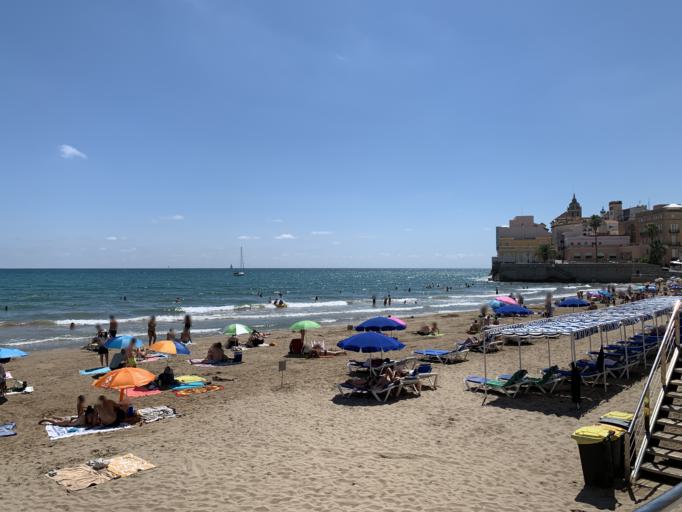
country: ES
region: Catalonia
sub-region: Provincia de Barcelona
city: Sitges
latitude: 41.2363
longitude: 1.8151
